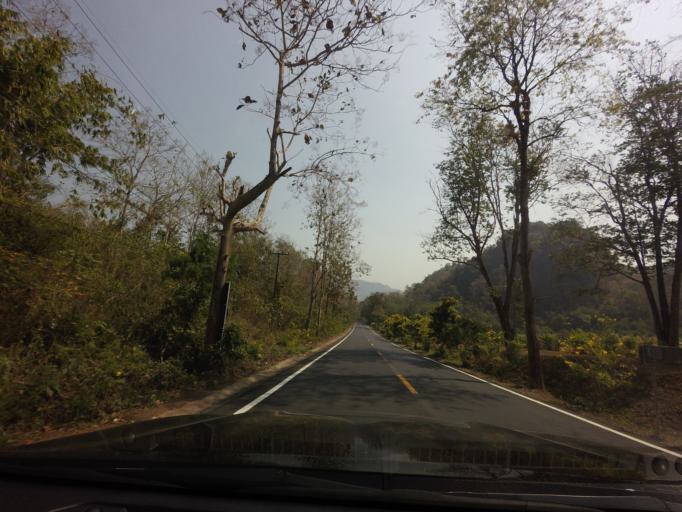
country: TH
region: Kanchanaburi
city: Thong Pha Phum
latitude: 14.7788
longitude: 98.5907
